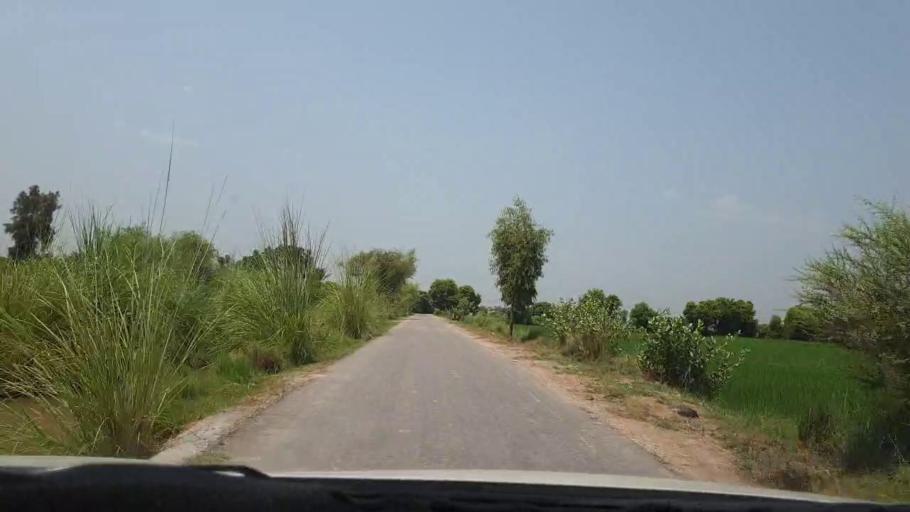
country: PK
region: Sindh
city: Radhan
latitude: 27.2397
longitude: 68.0143
